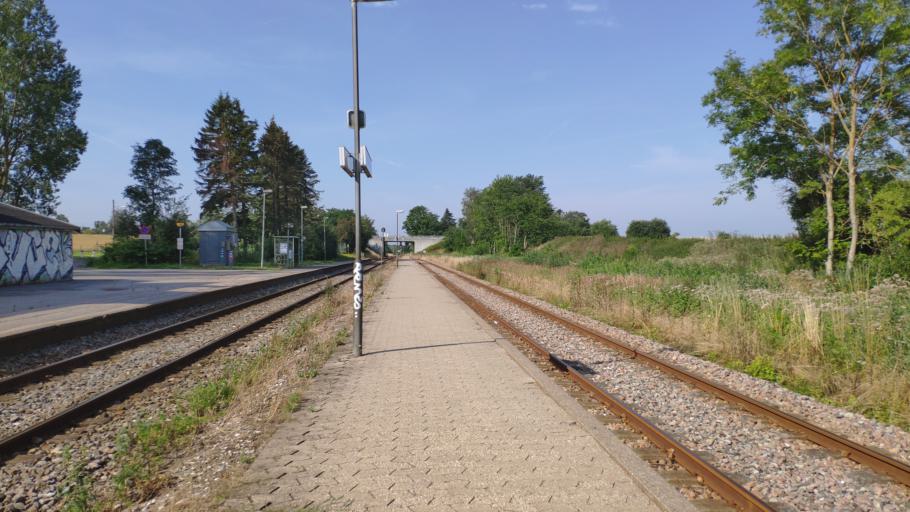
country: DK
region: Capital Region
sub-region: Hillerod Kommune
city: Hillerod
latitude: 55.8936
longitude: 12.2797
